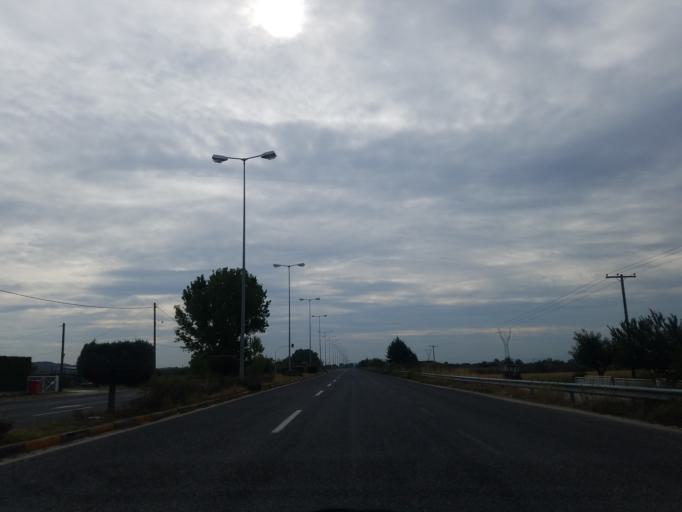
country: GR
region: Thessaly
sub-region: Trikala
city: Vasiliki
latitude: 39.6343
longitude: 21.6997
